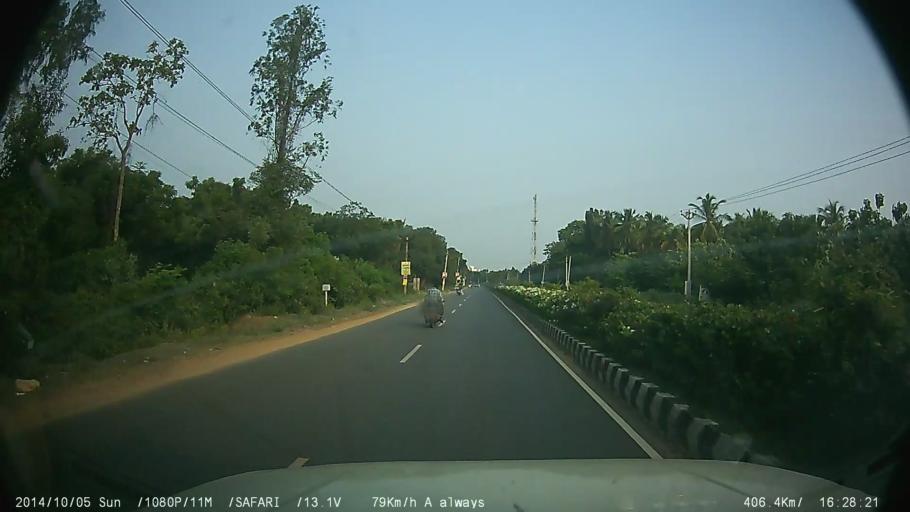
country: IN
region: Tamil Nadu
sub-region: Kancheepuram
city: Vengavasal
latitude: 12.7955
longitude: 80.2067
